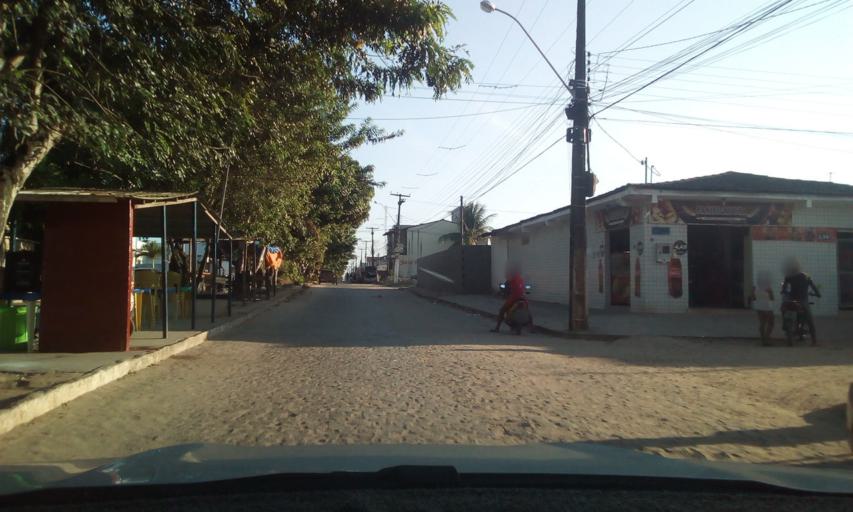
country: BR
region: Paraiba
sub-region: Bayeux
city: Bayeux
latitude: -7.1769
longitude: -34.9327
